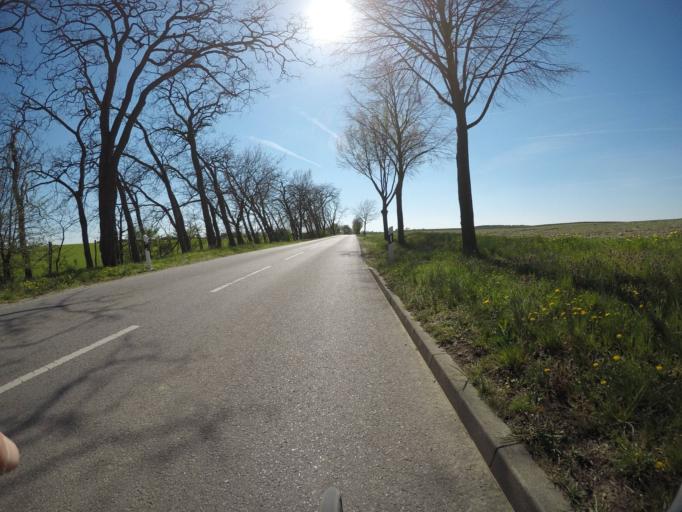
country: DE
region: Brandenburg
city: Protzel
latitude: 52.5635
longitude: 13.9658
